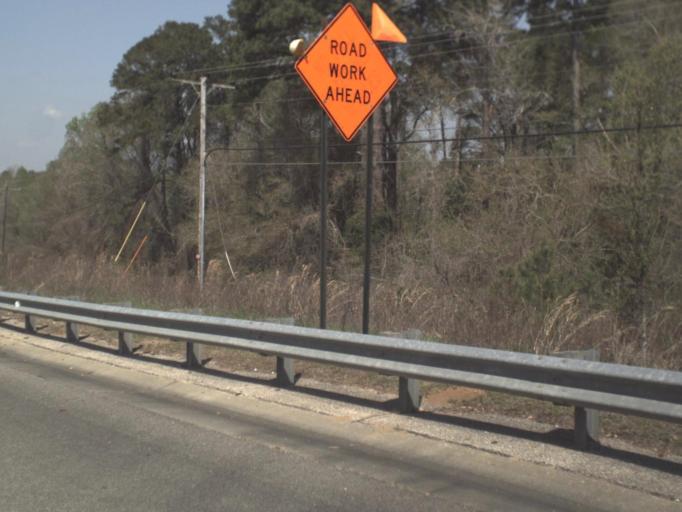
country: US
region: Florida
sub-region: Liberty County
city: Bristol
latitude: 30.4317
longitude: -84.9935
